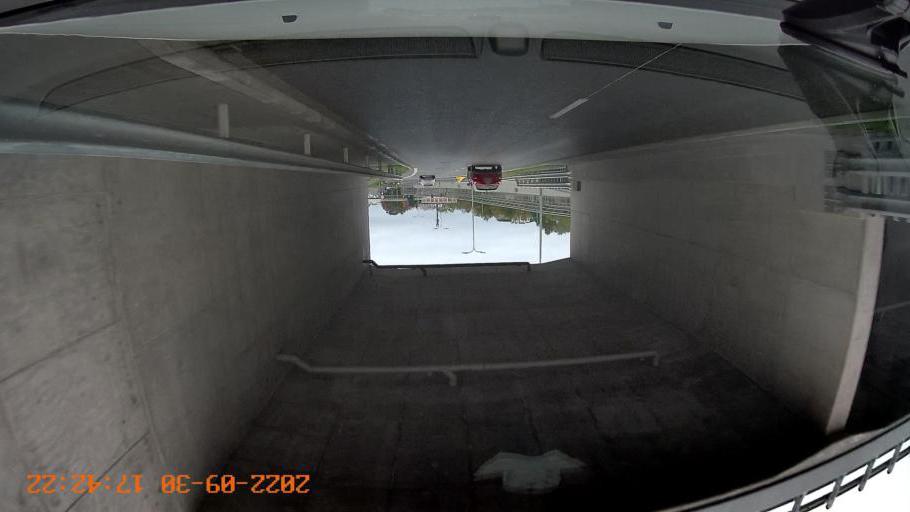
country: PL
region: Lesser Poland Voivodeship
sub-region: Krakow
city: Krakow
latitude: 50.0246
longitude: 19.9200
